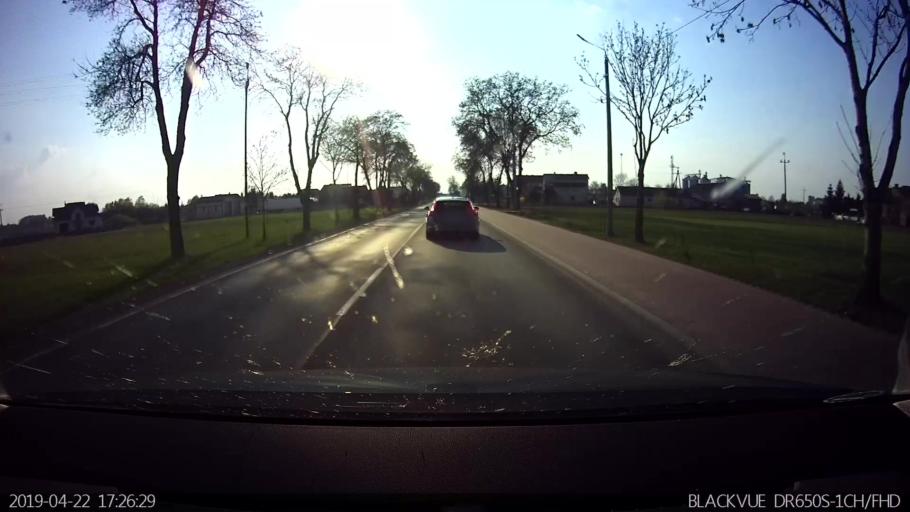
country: PL
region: Masovian Voivodeship
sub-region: Powiat sokolowski
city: Sokolow Podlaski
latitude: 52.3951
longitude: 22.2760
